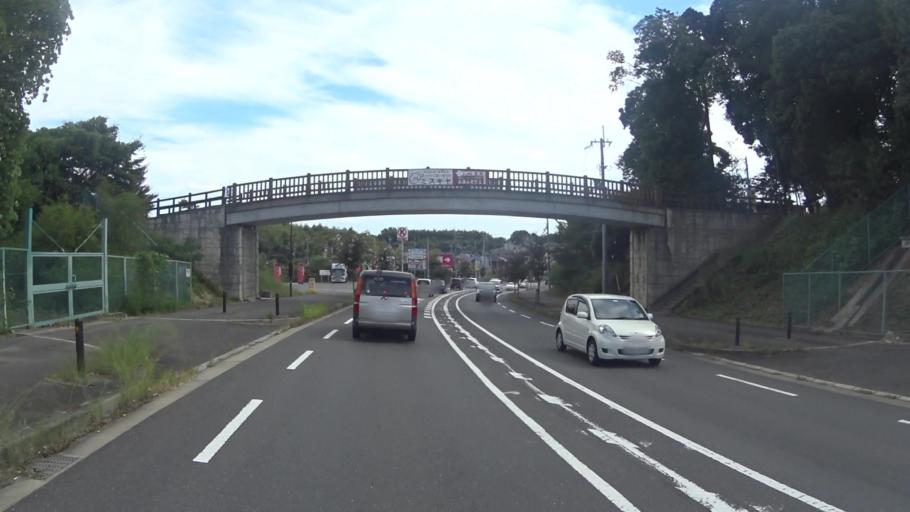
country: JP
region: Kyoto
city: Yawata
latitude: 34.8504
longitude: 135.7110
